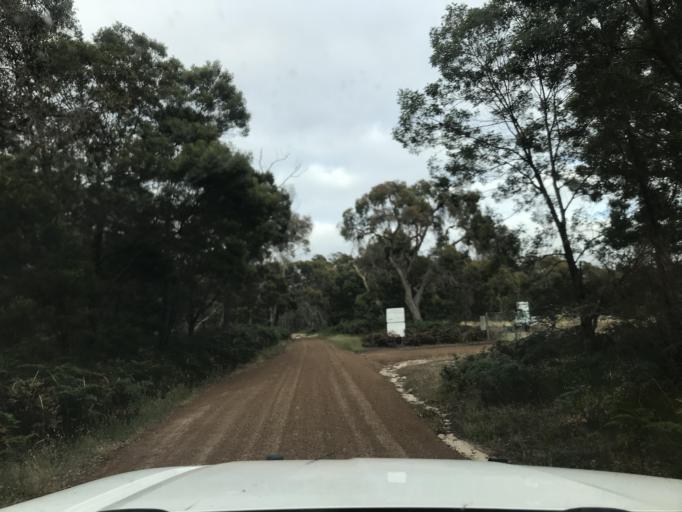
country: AU
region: South Australia
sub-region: Wattle Range
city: Penola
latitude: -37.2795
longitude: 141.3835
